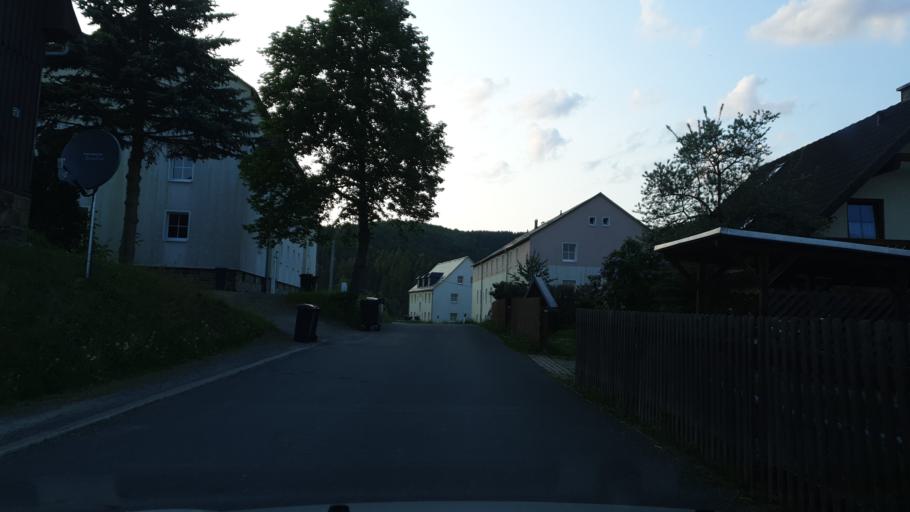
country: DE
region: Saxony
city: Klingenthal
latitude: 50.3800
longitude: 12.4598
